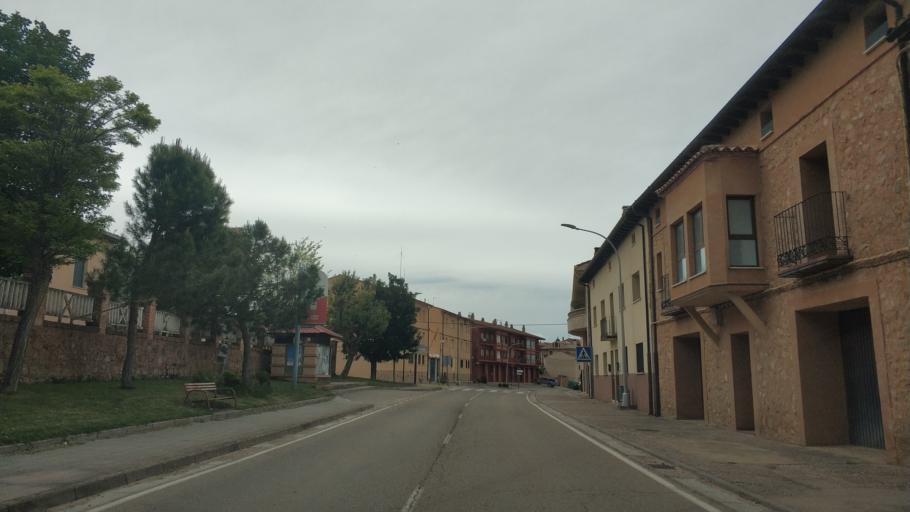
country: ES
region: Castille and Leon
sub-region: Provincia de Soria
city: Berlanga de Duero
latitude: 41.4643
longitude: -2.8625
